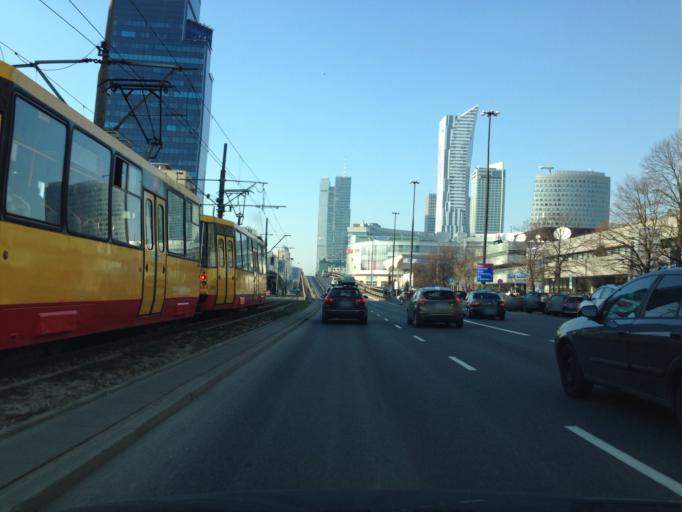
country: PL
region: Masovian Voivodeship
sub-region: Warszawa
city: Warsaw
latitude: 52.2254
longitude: 21.0035
